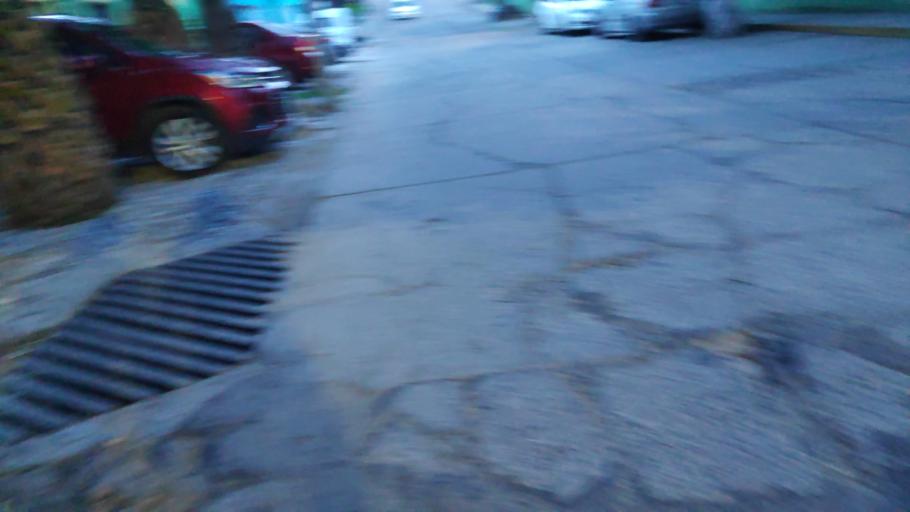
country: MX
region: Queretaro
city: La Canada
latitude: 20.6013
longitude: -100.3607
